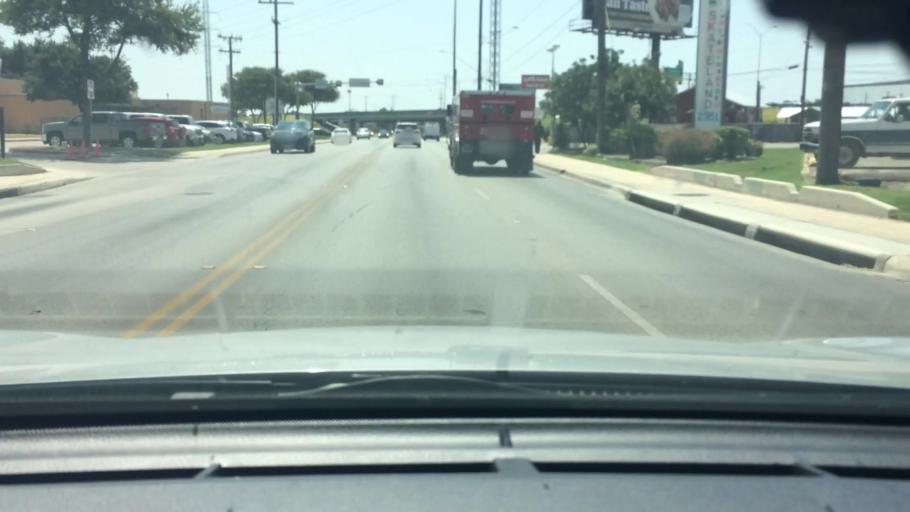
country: US
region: Texas
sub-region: Bexar County
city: San Antonio
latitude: 29.3618
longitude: -98.4378
